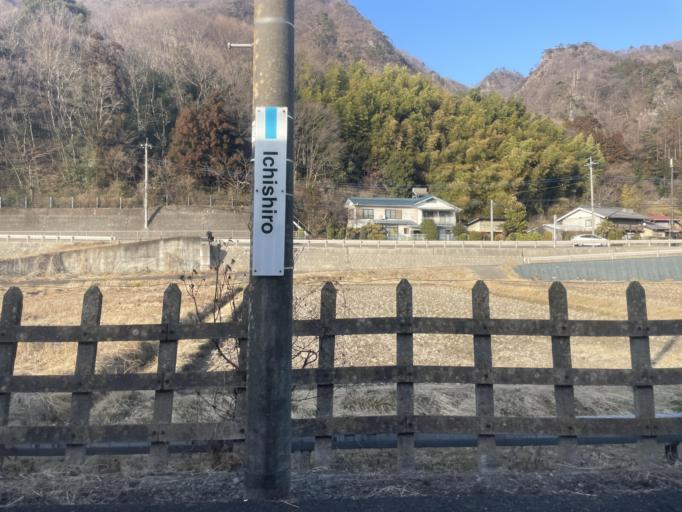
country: JP
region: Gunma
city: Nakanojomachi
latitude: 36.5711
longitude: 138.8819
